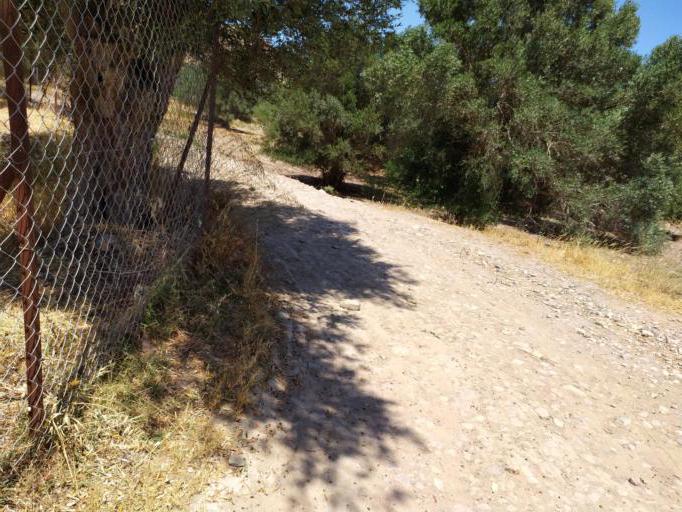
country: GR
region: Crete
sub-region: Nomos Irakleiou
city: Agioi Deka
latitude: 35.0584
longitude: 24.9515
